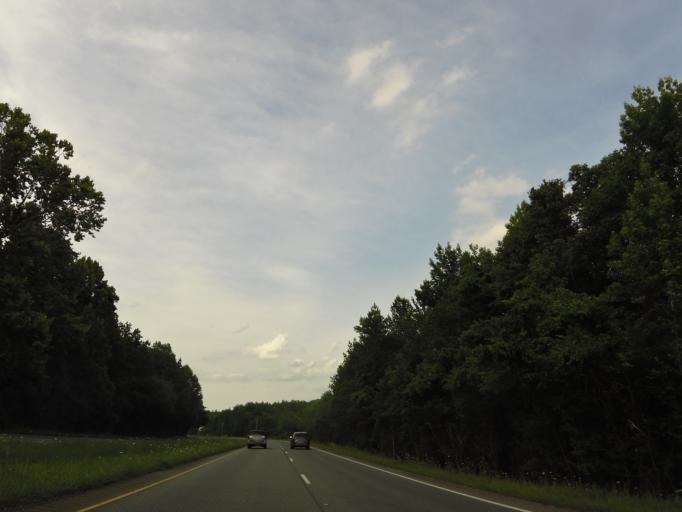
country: US
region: Tennessee
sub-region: Humphreys County
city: Johnsonville
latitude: 36.0597
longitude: -87.8923
